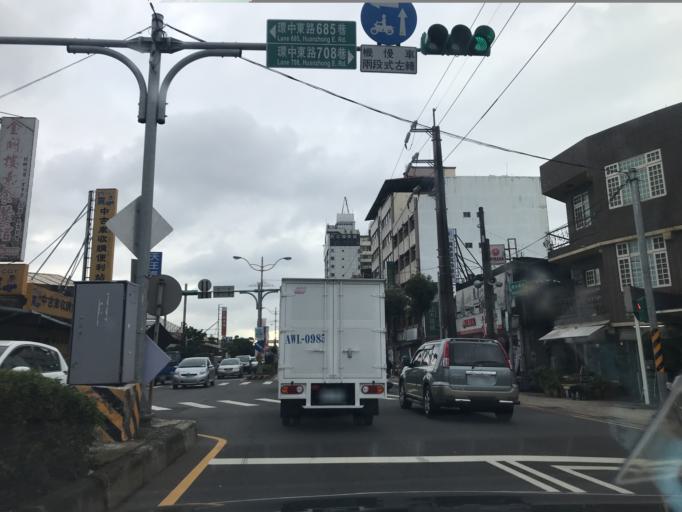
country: TW
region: Taiwan
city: Taoyuan City
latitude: 24.9554
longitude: 121.2458
